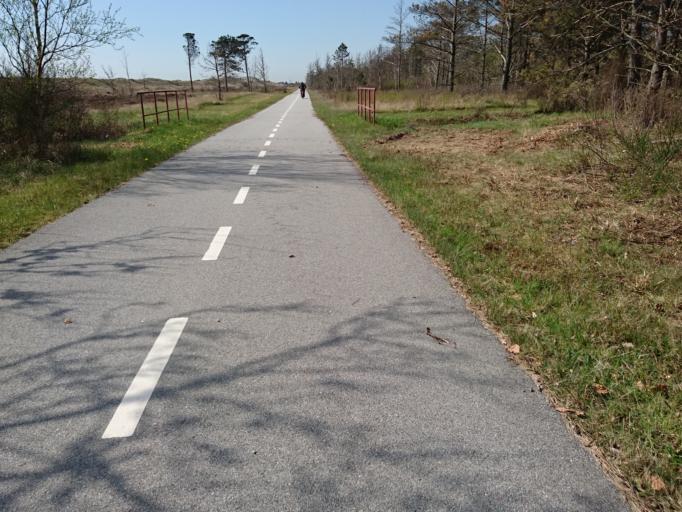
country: DK
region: North Denmark
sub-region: Frederikshavn Kommune
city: Skagen
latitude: 57.6383
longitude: 10.4577
